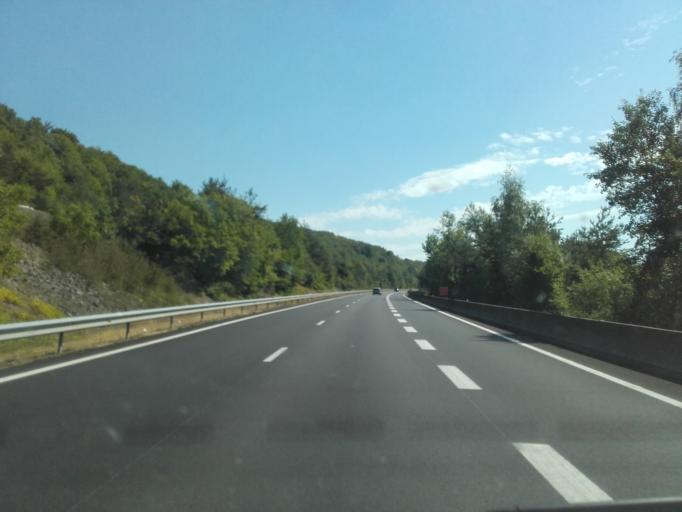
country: FR
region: Bourgogne
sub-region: Departement de la Cote-d'Or
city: Savigny-les-Beaune
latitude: 47.1441
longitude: 4.7014
